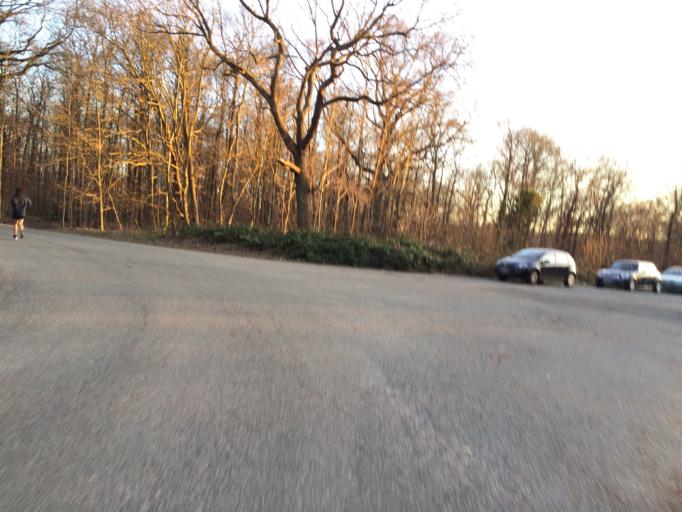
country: FR
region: Ile-de-France
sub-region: Departement des Hauts-de-Seine
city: Clamart
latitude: 48.7963
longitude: 2.2490
